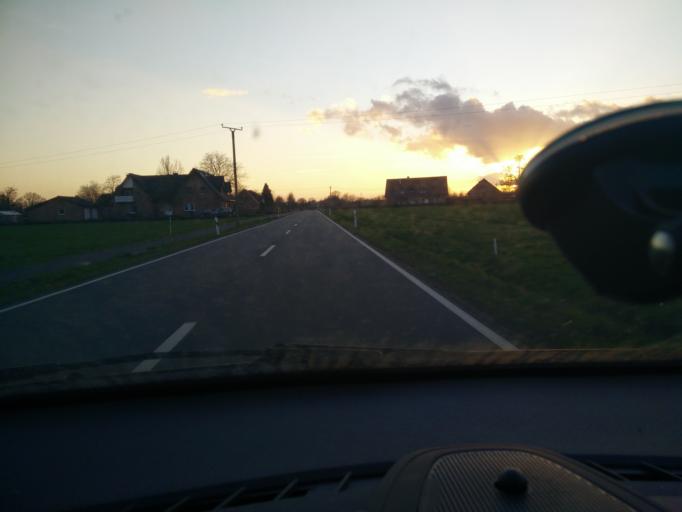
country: DE
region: North Rhine-Westphalia
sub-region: Regierungsbezirk Munster
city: Raesfeld
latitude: 51.7753
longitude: 6.8575
